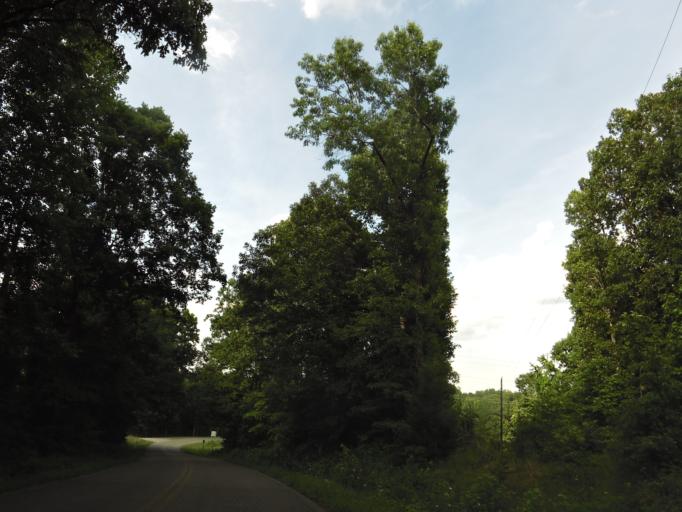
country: US
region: Tennessee
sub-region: Benton County
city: Camden
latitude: 36.0591
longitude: -88.1630
